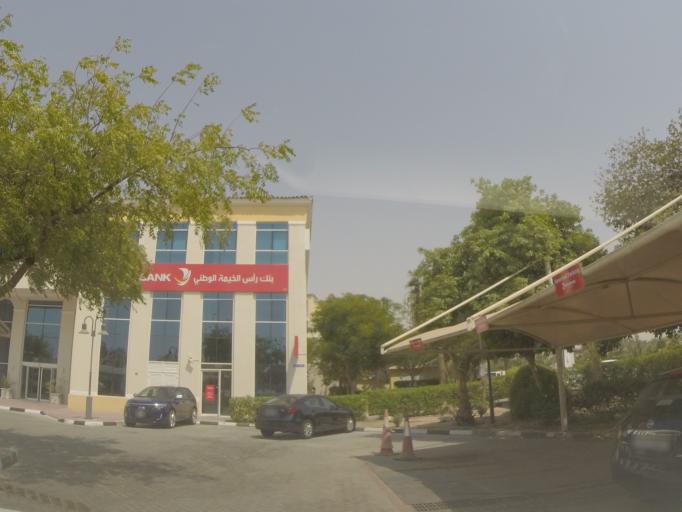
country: AE
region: Dubai
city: Dubai
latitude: 25.0021
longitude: 55.1603
